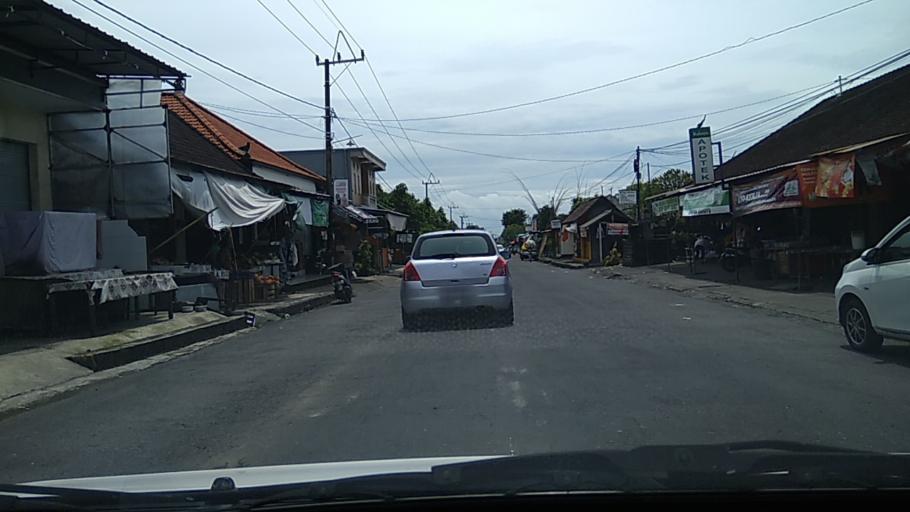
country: ID
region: Bali
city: Banjar Jagasatru
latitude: -8.5626
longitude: 115.1362
